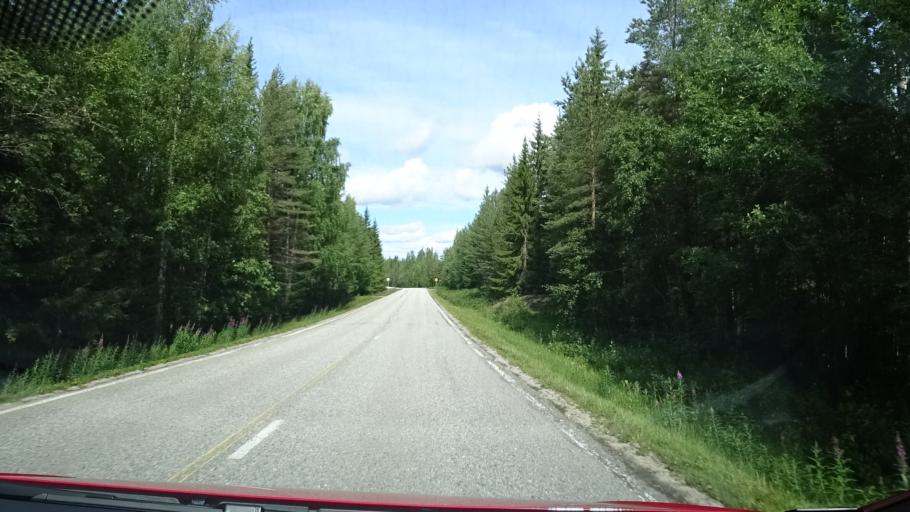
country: FI
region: Kainuu
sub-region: Kehys-Kainuu
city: Kuhmo
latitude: 64.4394
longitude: 29.8058
